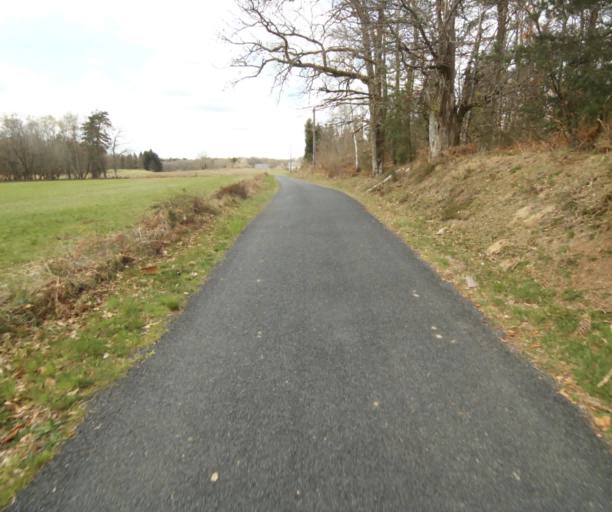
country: FR
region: Limousin
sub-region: Departement de la Correze
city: Argentat
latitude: 45.2168
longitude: 1.9257
